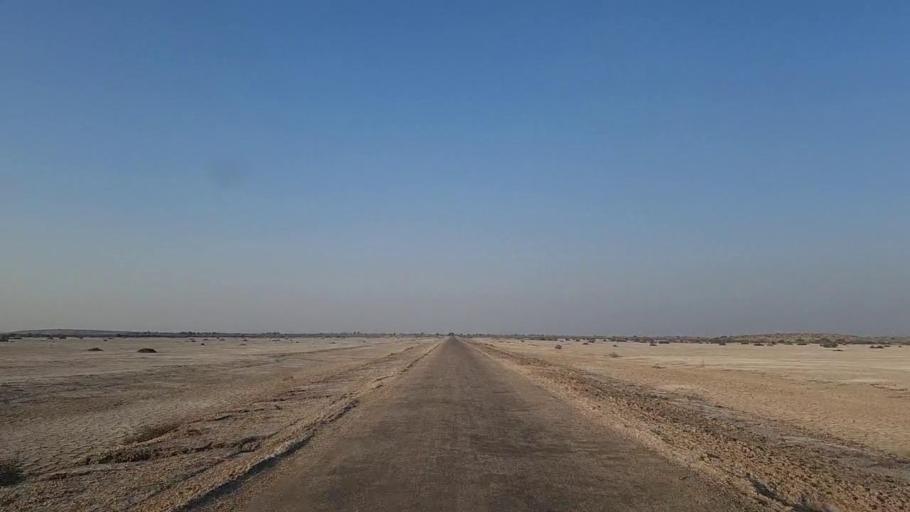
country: PK
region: Sindh
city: Jam Sahib
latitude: 26.3141
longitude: 68.6688
